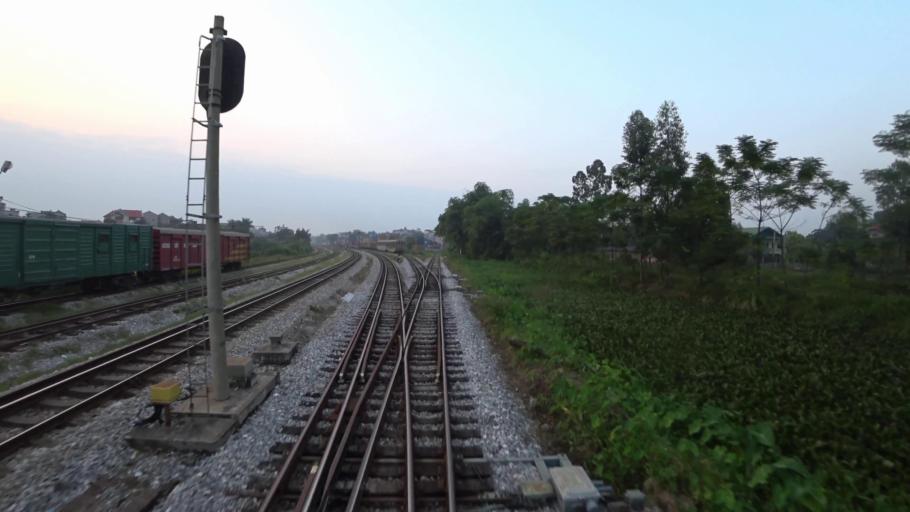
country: VN
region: Ha Noi
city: Dong Anh
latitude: 21.1519
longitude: 105.8542
